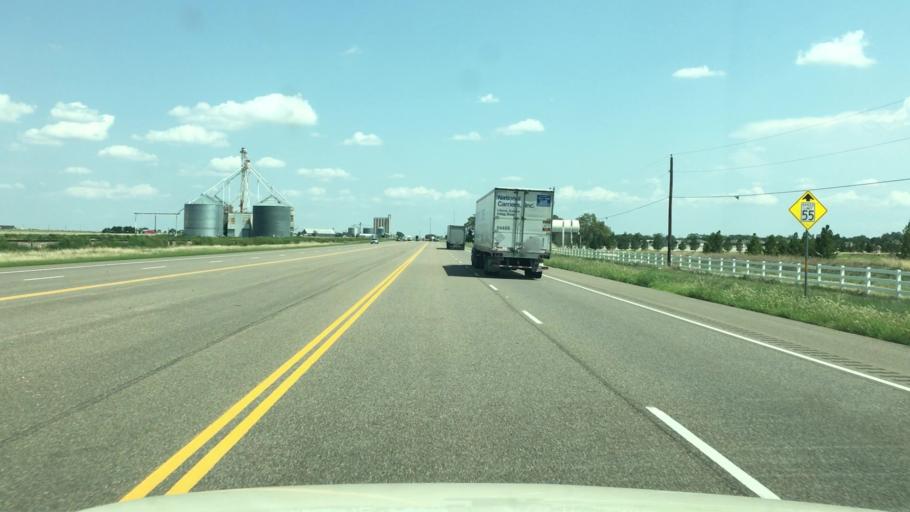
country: US
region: Texas
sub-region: Armstrong County
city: Claude
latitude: 35.1183
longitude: -101.3783
